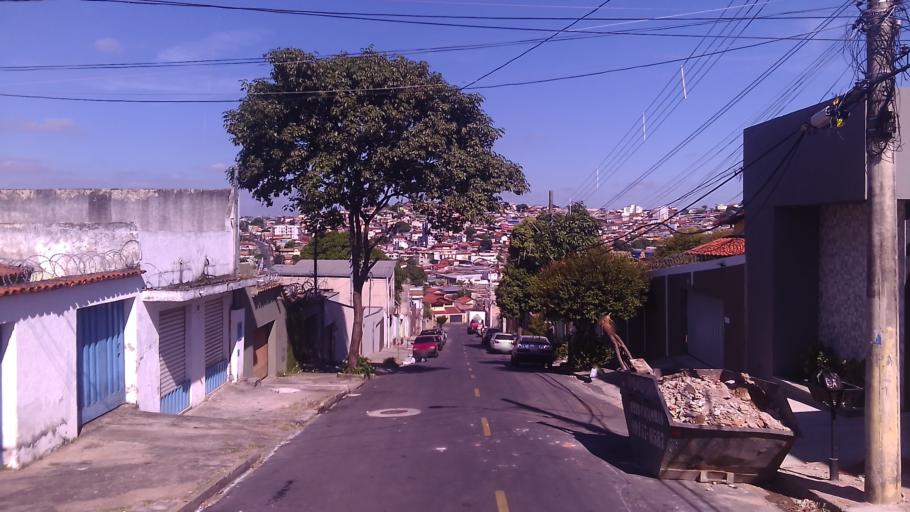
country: BR
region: Minas Gerais
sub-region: Contagem
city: Contagem
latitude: -19.9031
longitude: -44.0147
